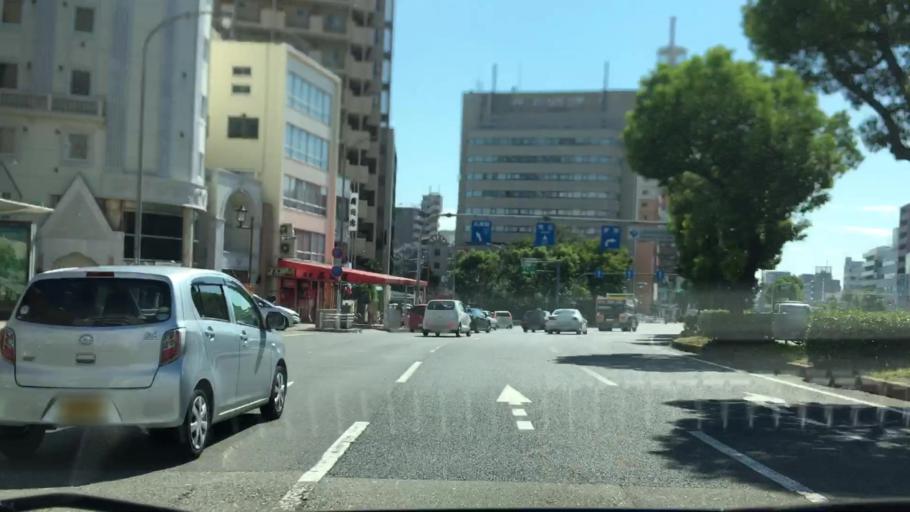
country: JP
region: Hyogo
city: Kobe
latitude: 34.6768
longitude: 135.1708
